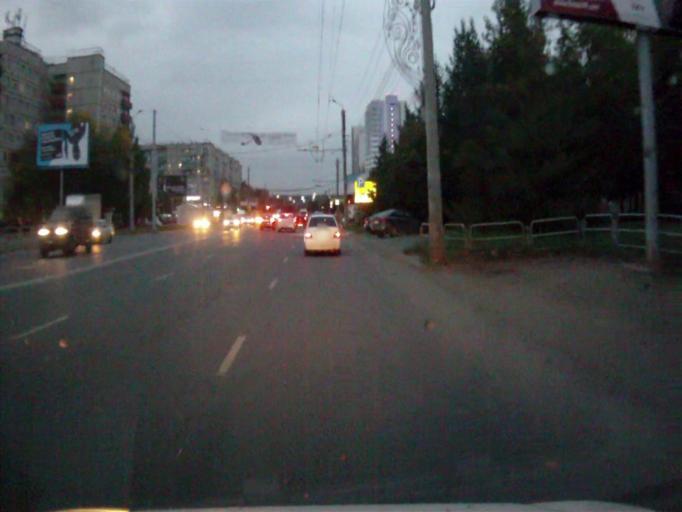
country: RU
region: Chelyabinsk
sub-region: Gorod Chelyabinsk
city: Chelyabinsk
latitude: 55.1806
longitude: 61.3326
